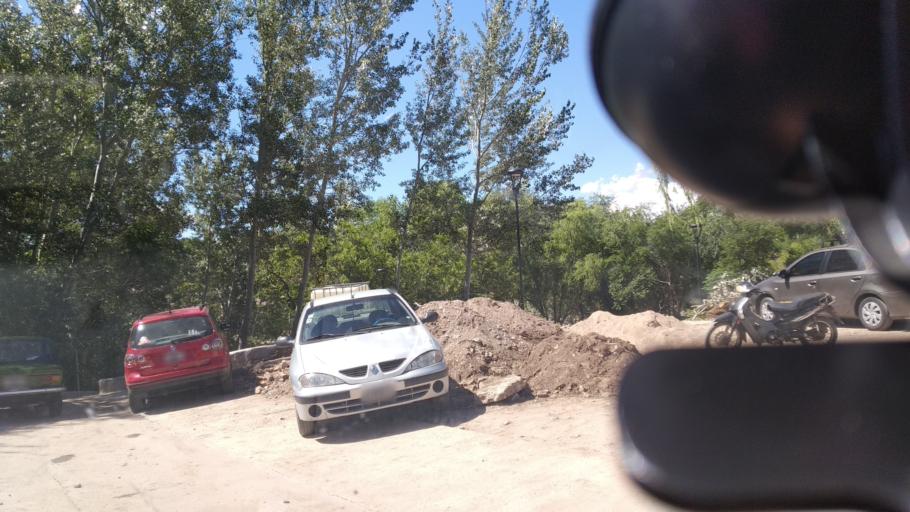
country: AR
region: Cordoba
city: Mina Clavero
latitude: -31.7228
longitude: -65.0124
